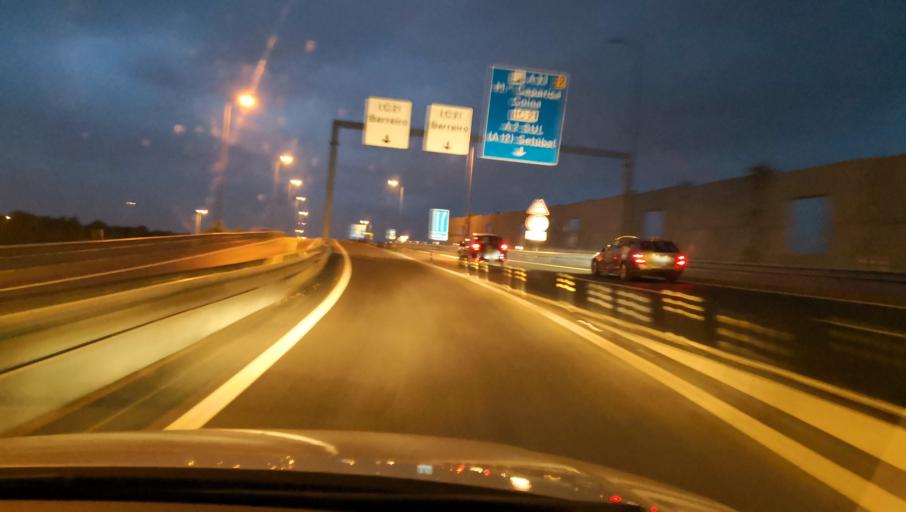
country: PT
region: Setubal
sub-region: Barreiro
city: Santo Antonio da Charneca
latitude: 38.6030
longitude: -9.0192
